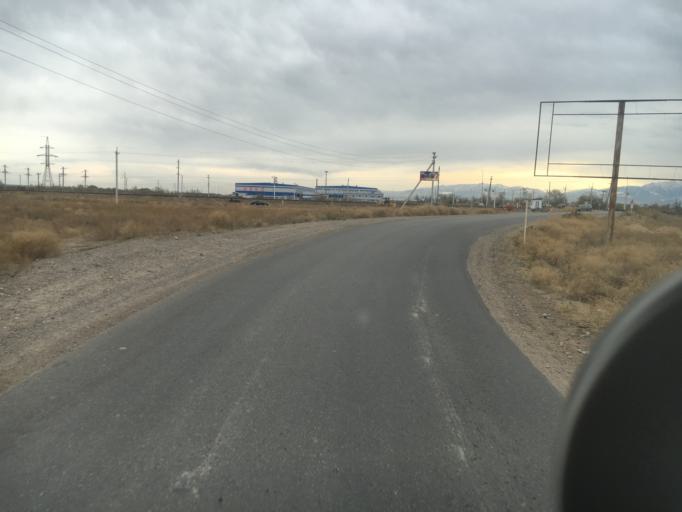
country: KZ
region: Almaty Oblysy
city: Energeticheskiy
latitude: 43.5855
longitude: 77.0860
